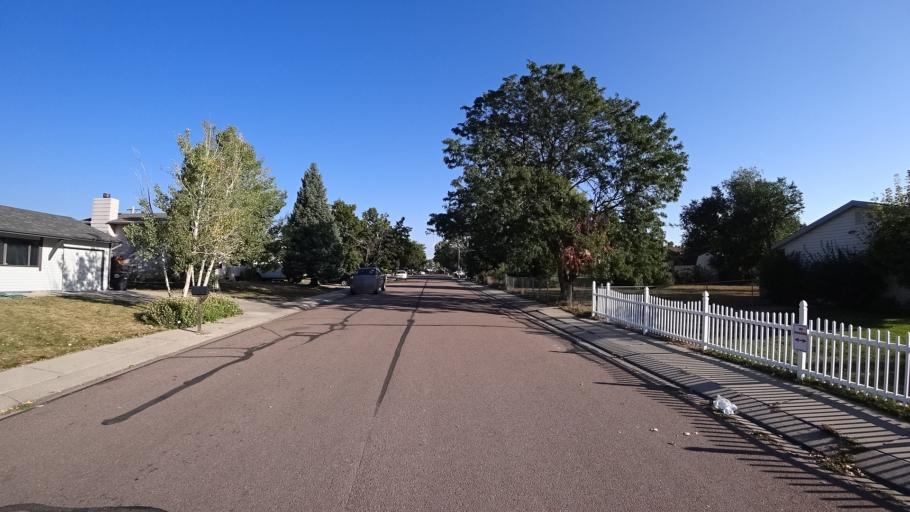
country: US
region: Colorado
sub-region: El Paso County
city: Cimarron Hills
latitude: 38.8942
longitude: -104.7475
